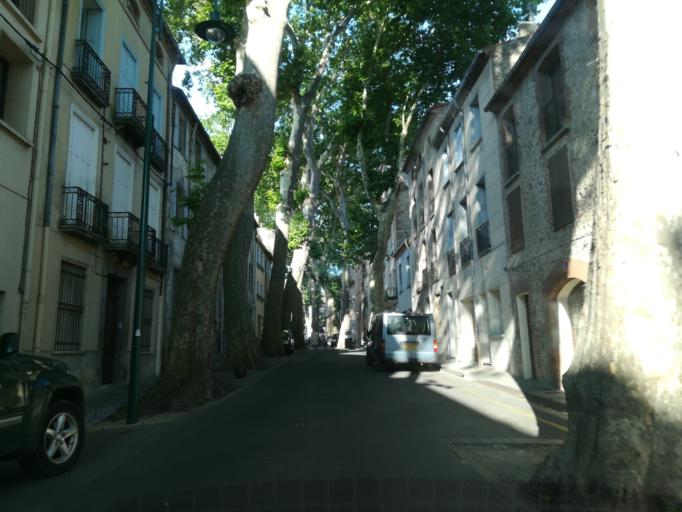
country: FR
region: Languedoc-Roussillon
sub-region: Departement des Pyrenees-Orientales
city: Ceret
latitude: 42.4842
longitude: 2.7490
